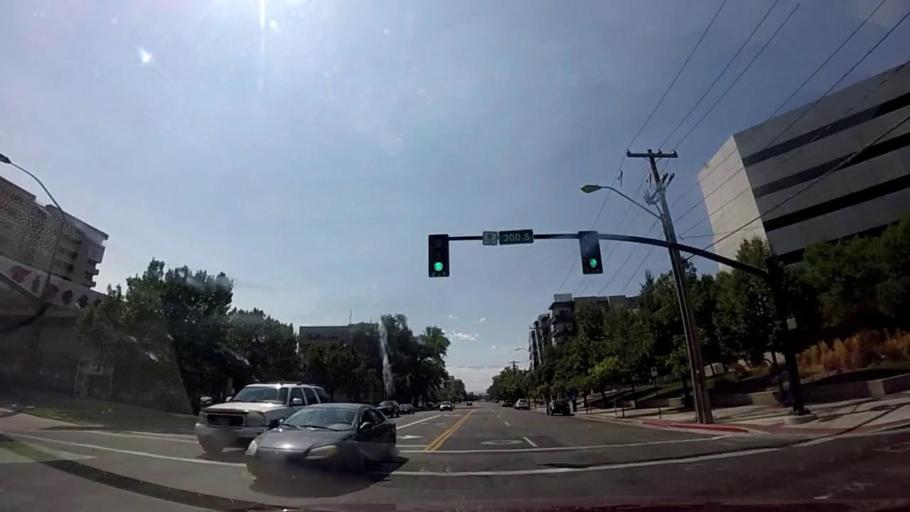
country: US
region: Utah
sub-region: Salt Lake County
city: Salt Lake City
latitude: 40.7627
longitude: -111.8855
